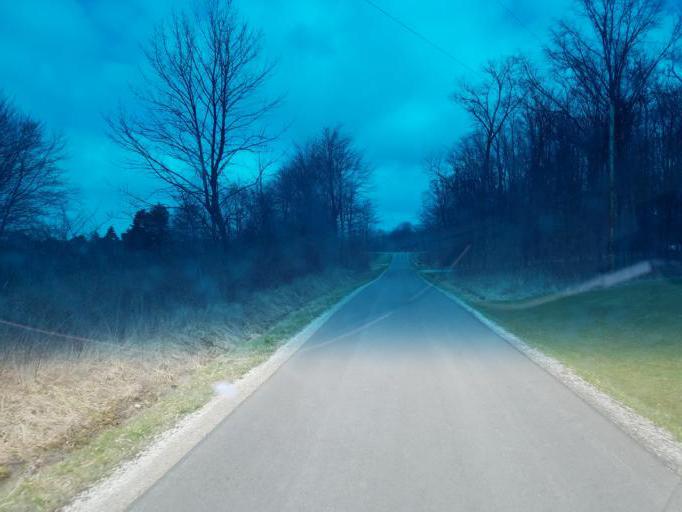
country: US
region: Ohio
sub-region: Crawford County
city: Galion
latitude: 40.7825
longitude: -82.8098
